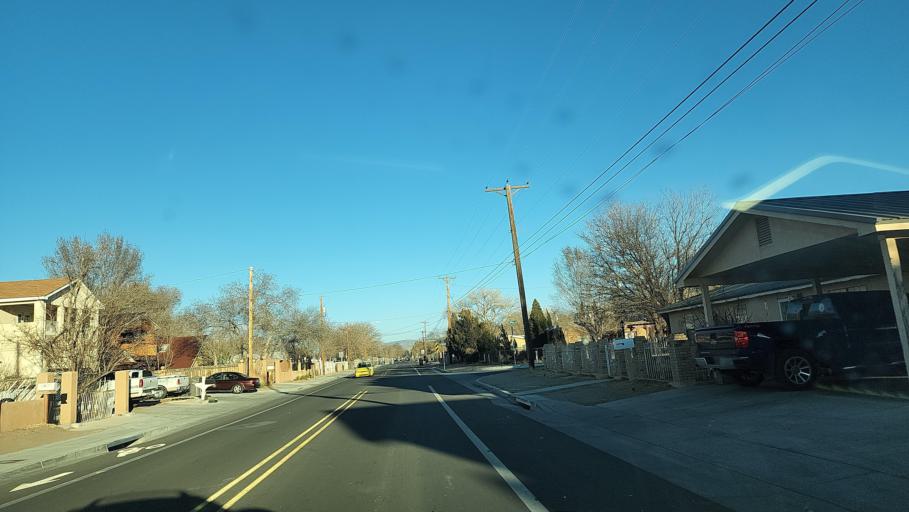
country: US
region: New Mexico
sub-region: Bernalillo County
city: South Valley
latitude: 35.0305
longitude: -106.7000
